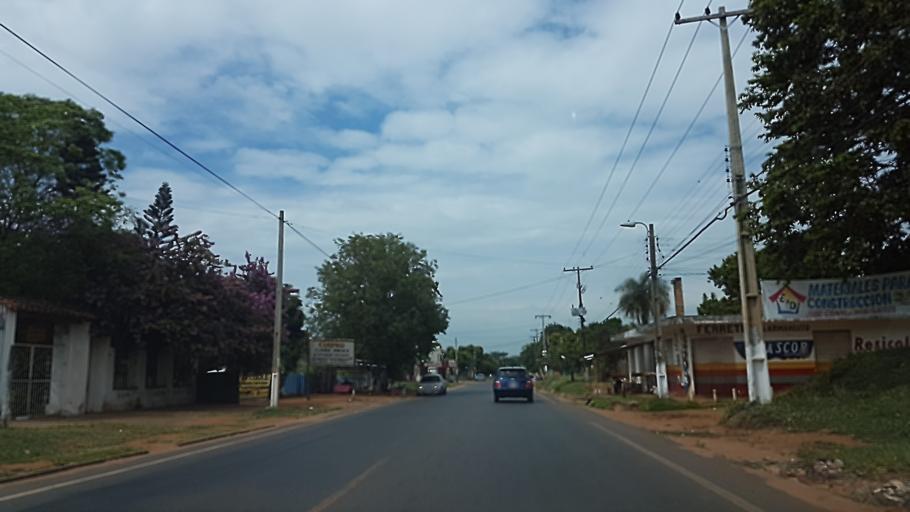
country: PY
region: Central
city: Capiata
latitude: -25.3794
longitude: -57.4586
